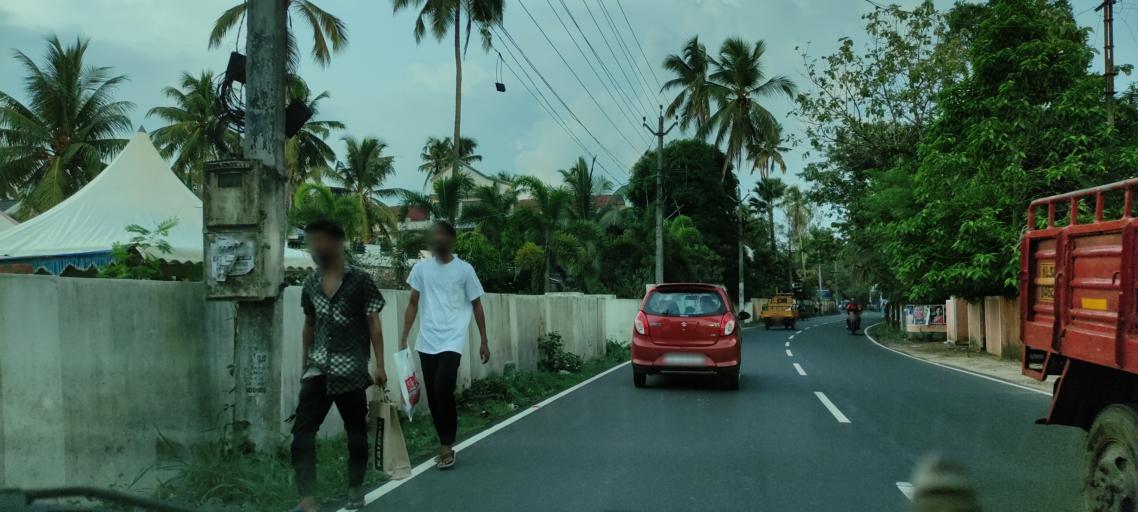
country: IN
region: Kerala
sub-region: Alappuzha
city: Kutiatodu
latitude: 9.8323
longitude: 76.3401
